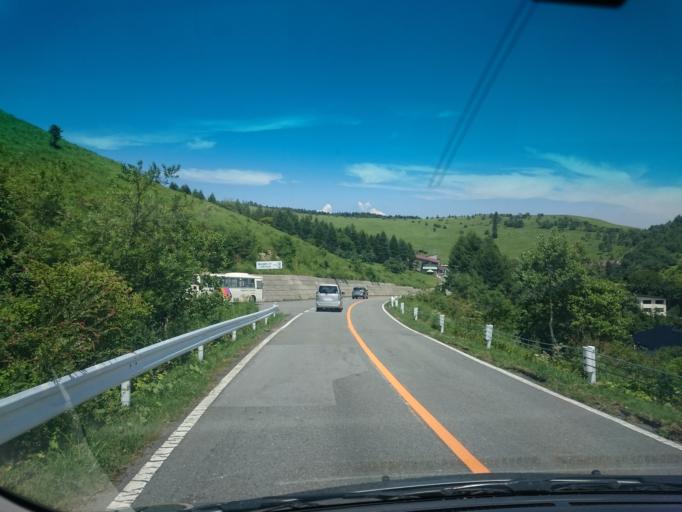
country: JP
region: Nagano
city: Suwa
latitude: 36.0992
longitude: 138.2106
